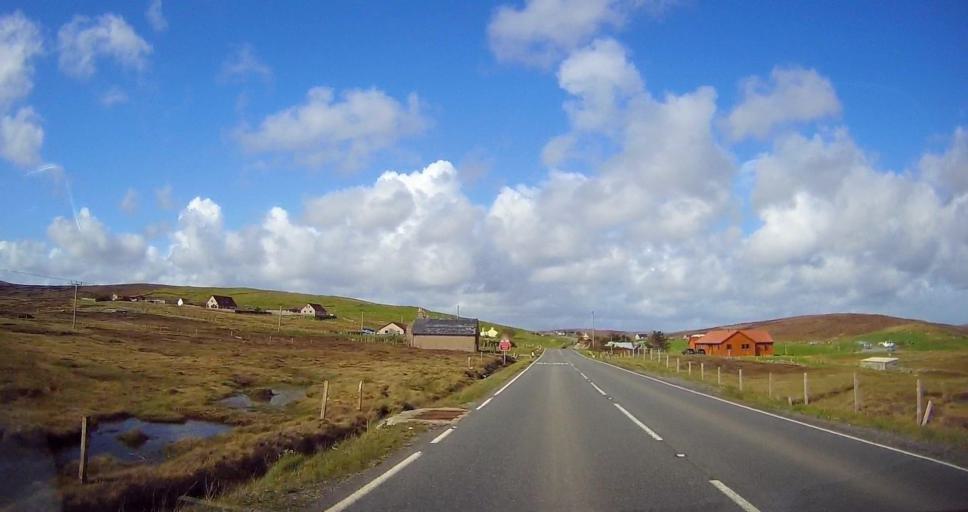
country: GB
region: Scotland
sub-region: Shetland Islands
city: Lerwick
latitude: 60.2335
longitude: -1.2348
